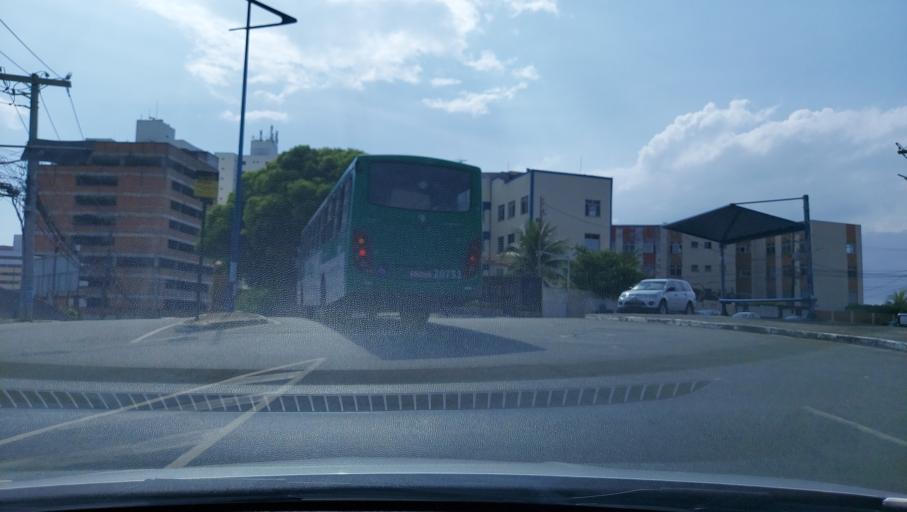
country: BR
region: Bahia
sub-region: Salvador
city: Salvador
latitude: -12.9808
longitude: -38.4458
